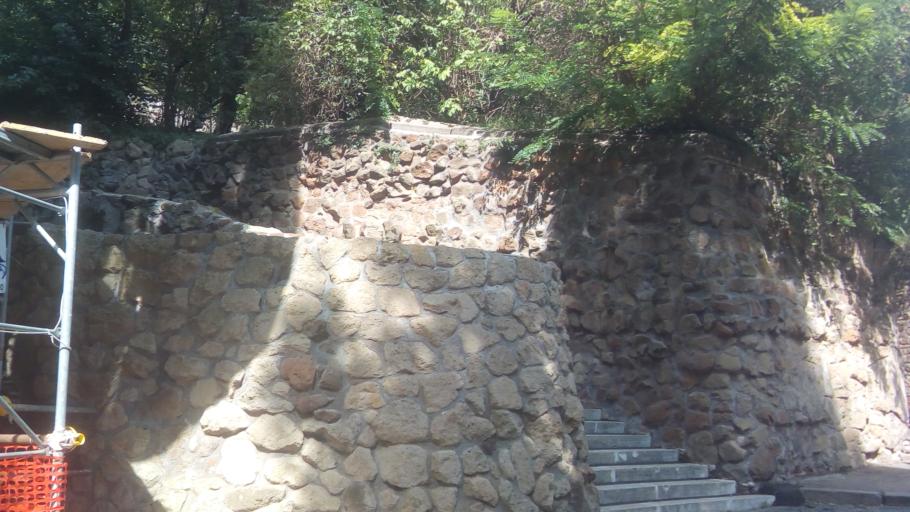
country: VA
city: Vatican City
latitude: 41.8865
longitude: 12.4683
